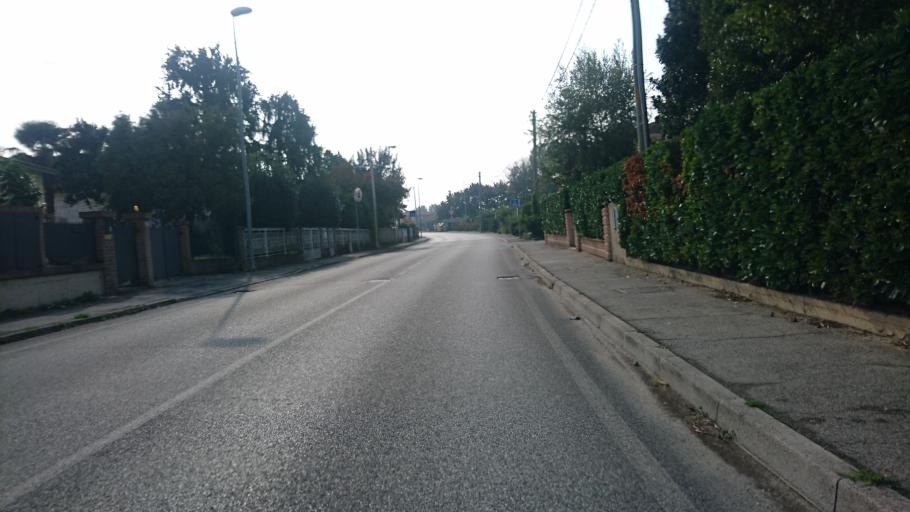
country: IT
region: Veneto
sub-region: Provincia di Rovigo
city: Rovigo
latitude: 45.0586
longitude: 11.7814
